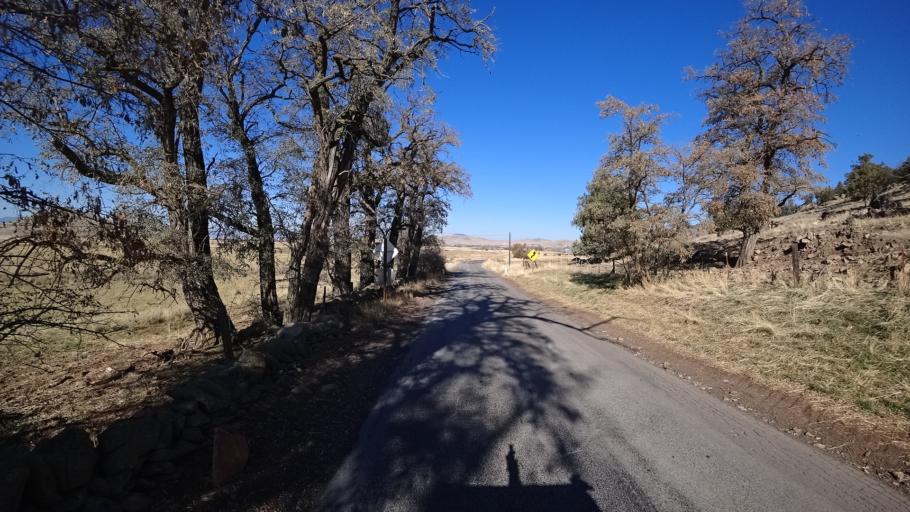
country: US
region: California
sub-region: Siskiyou County
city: Montague
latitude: 41.6914
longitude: -122.3726
